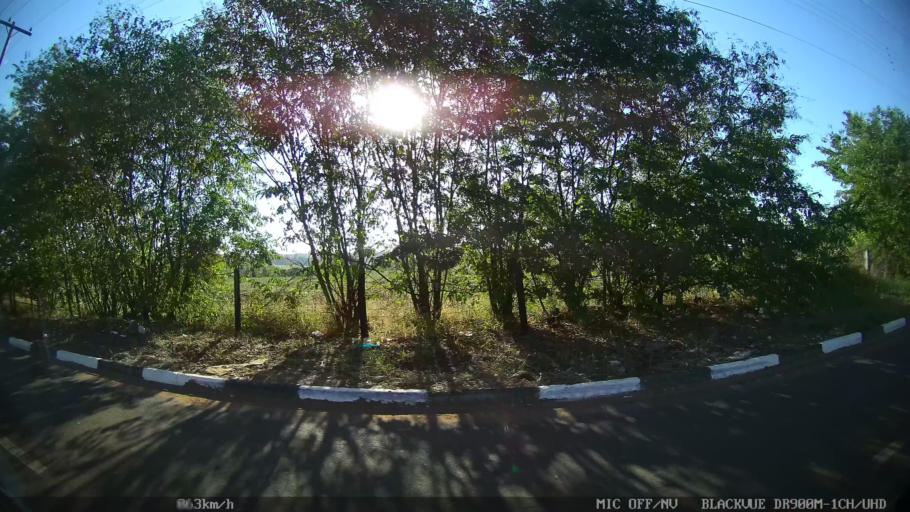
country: BR
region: Sao Paulo
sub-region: Franca
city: Franca
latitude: -20.5093
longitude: -47.3732
